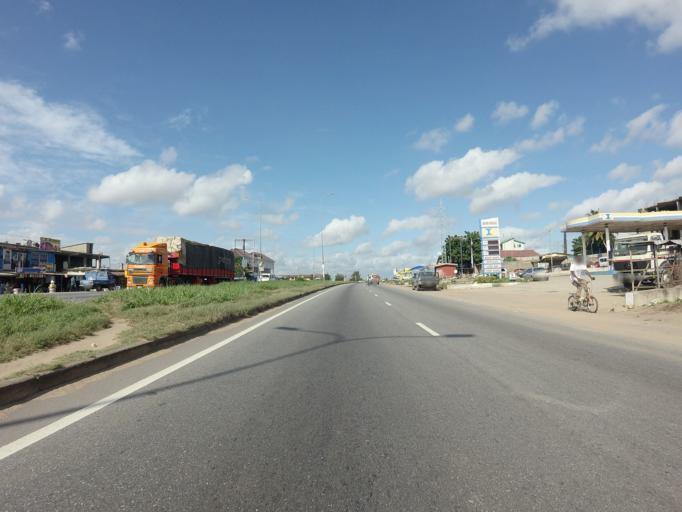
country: GH
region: Central
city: Kasoa
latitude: 5.5361
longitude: -0.4089
